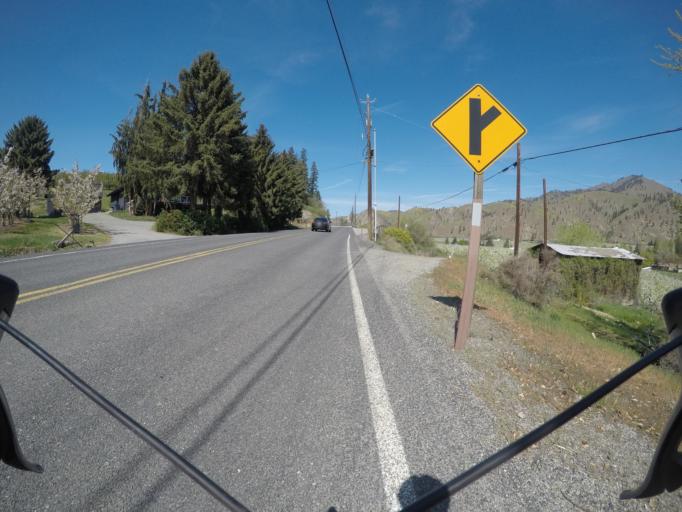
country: US
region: Washington
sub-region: Chelan County
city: Cashmere
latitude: 47.5251
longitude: -120.4997
